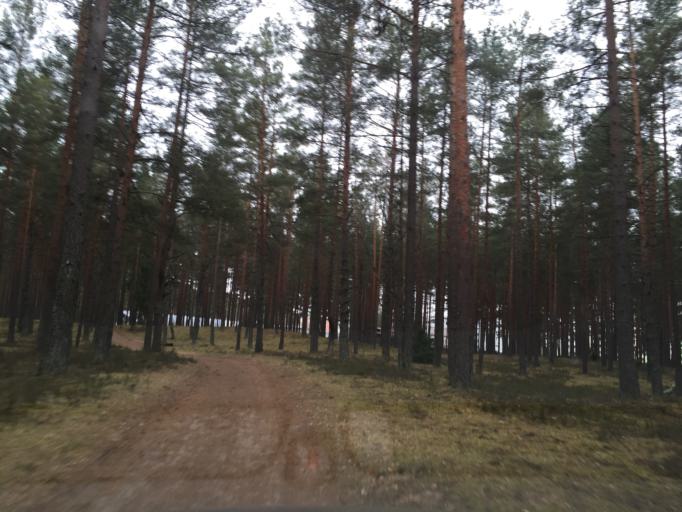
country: LV
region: Garkalne
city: Garkalne
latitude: 56.9669
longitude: 24.4317
